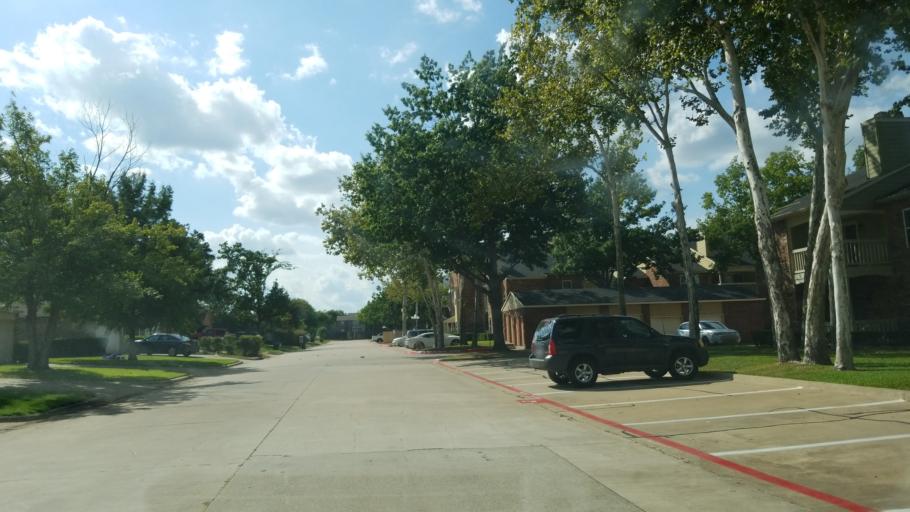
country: US
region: Texas
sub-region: Tarrant County
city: Euless
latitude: 32.8558
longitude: -97.0756
